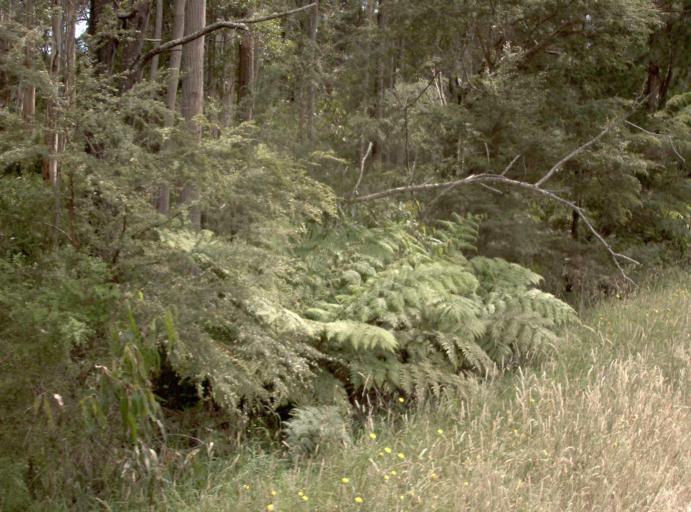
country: AU
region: Victoria
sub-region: Latrobe
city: Moe
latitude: -37.9407
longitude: 146.4007
